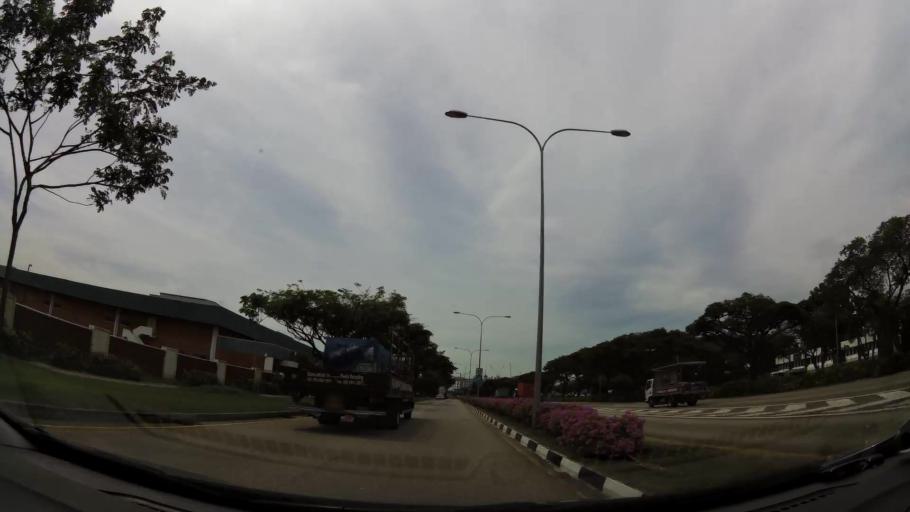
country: MY
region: Johor
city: Johor Bahru
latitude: 1.3222
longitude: 103.6754
